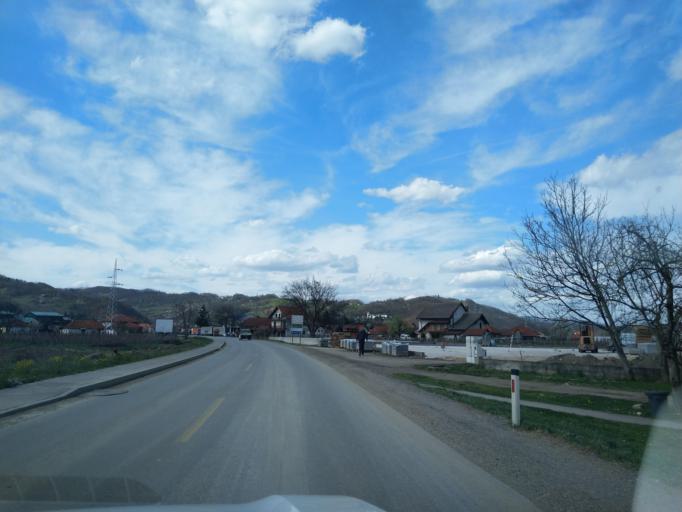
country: RS
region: Central Serbia
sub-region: Zlatiborski Okrug
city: Arilje
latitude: 43.7544
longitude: 20.1036
